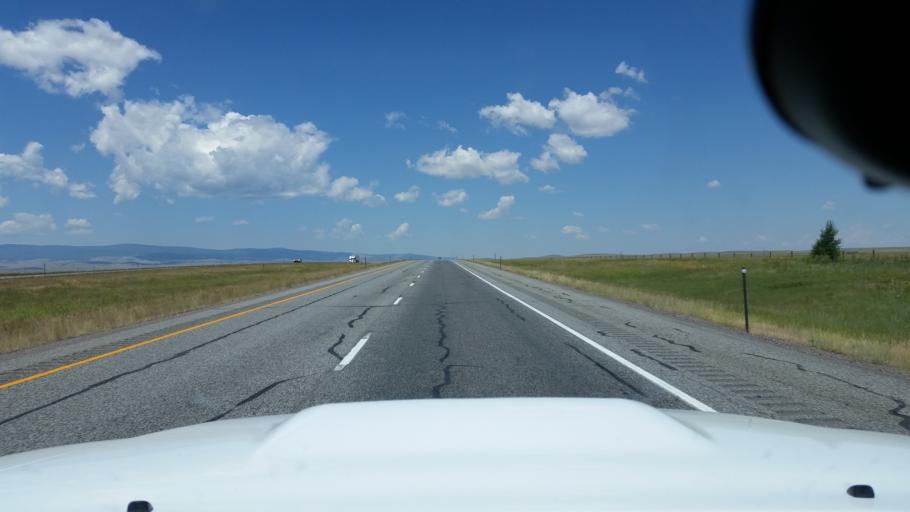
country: US
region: Wyoming
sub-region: Albany County
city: Laramie
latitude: 41.4146
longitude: -105.8472
